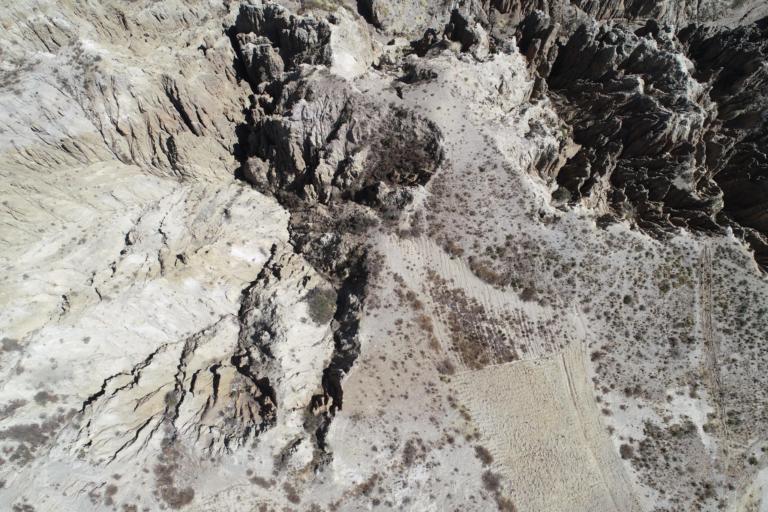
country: BO
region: La Paz
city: La Paz
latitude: -16.5948
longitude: -68.1304
